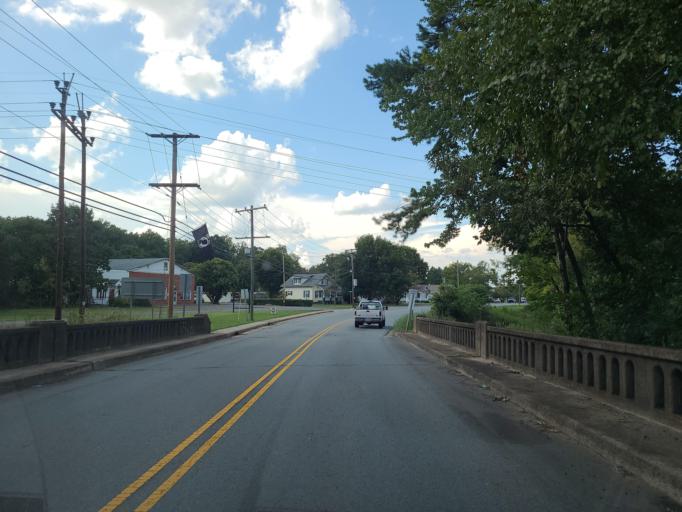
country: US
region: North Carolina
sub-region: Gaston County
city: Lowell
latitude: 35.2740
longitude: -81.0974
